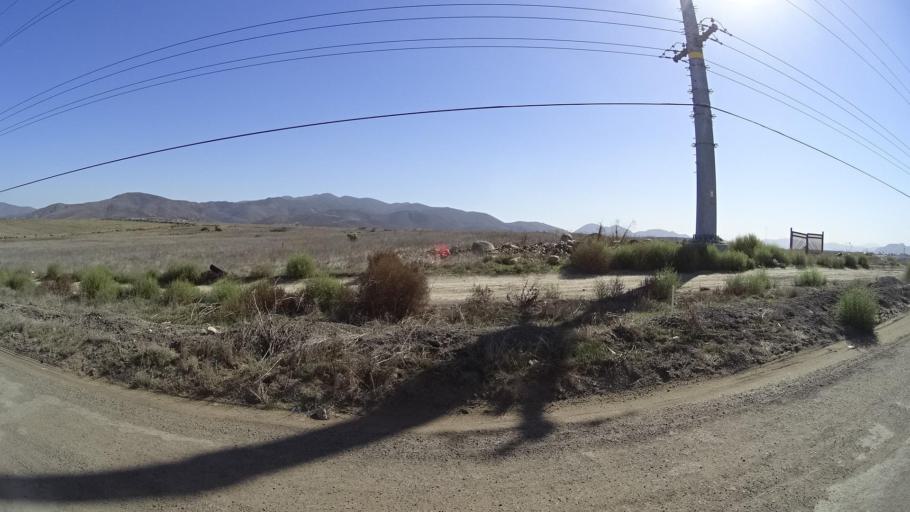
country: MX
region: Baja California
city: Tijuana
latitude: 32.5726
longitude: -116.9451
